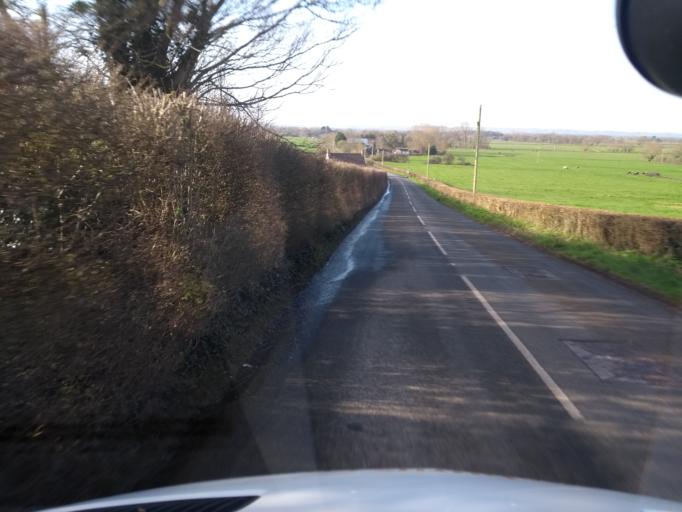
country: GB
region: England
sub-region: Somerset
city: Wedmore
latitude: 51.2074
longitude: -2.7997
